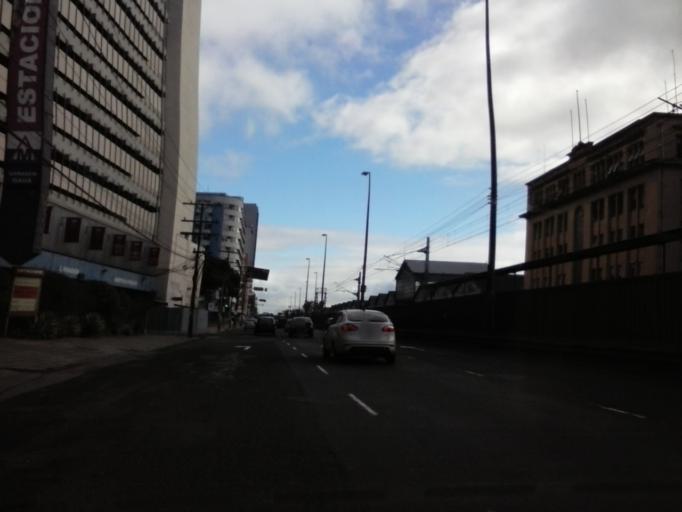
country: BR
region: Rio Grande do Sul
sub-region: Porto Alegre
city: Porto Alegre
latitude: -30.0271
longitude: -51.2304
